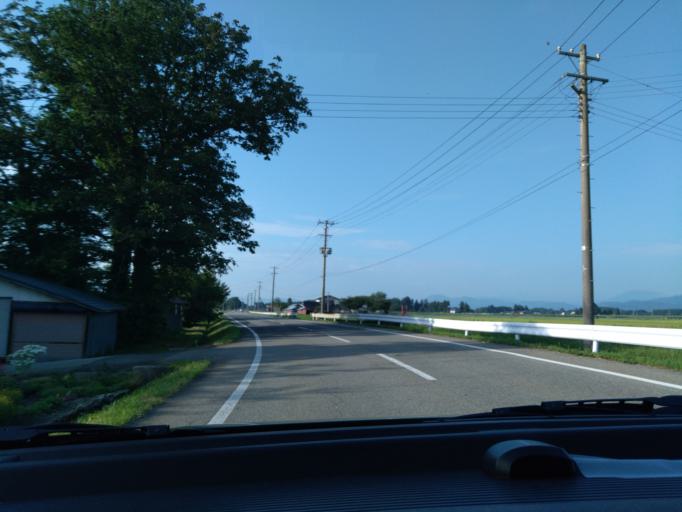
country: JP
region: Akita
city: Kakunodatemachi
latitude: 39.5283
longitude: 140.5585
